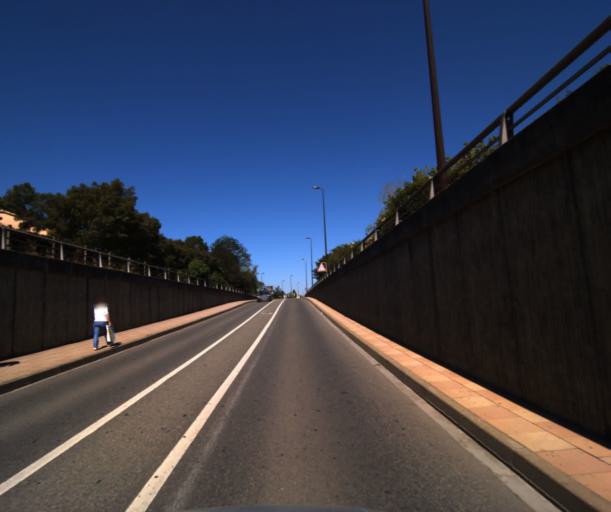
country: FR
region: Midi-Pyrenees
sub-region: Departement de la Haute-Garonne
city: Muret
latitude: 43.4678
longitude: 1.3258
